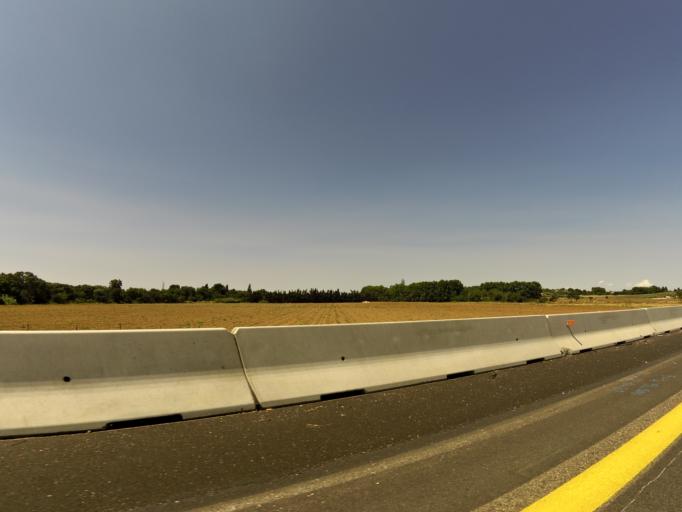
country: FR
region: Languedoc-Roussillon
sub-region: Departement de l'Herault
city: Saint-Aunes
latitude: 43.6262
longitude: 3.9627
